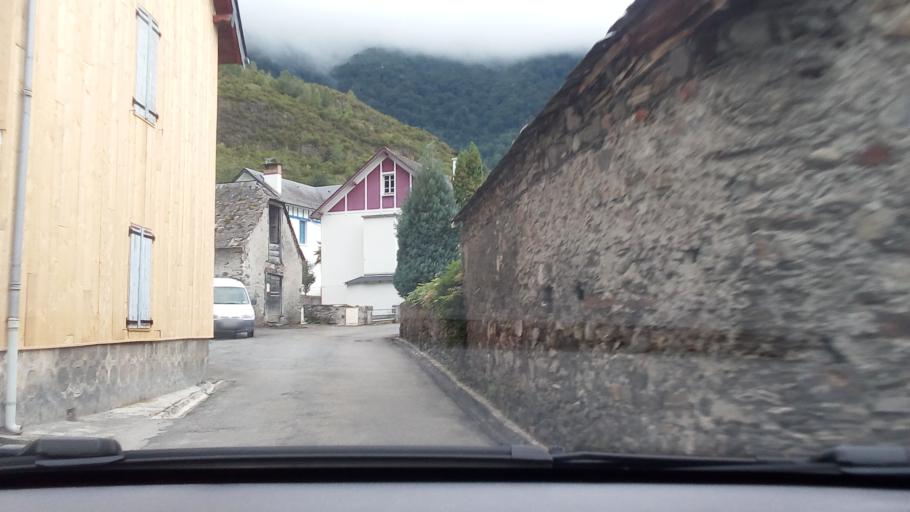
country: FR
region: Midi-Pyrenees
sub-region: Departement des Hautes-Pyrenees
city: Pierrefitte-Nestalas
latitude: 42.9542
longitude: -0.0584
